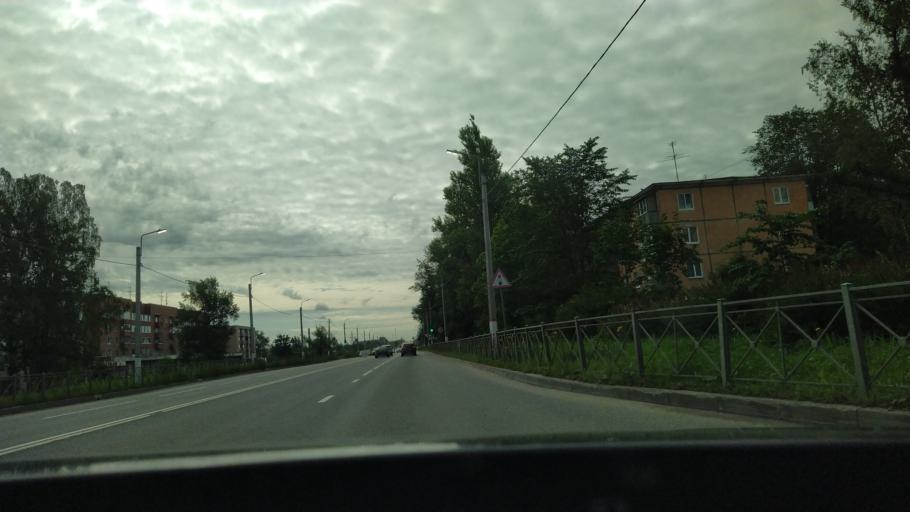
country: RU
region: Leningrad
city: Tosno
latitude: 59.5587
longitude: 30.8446
